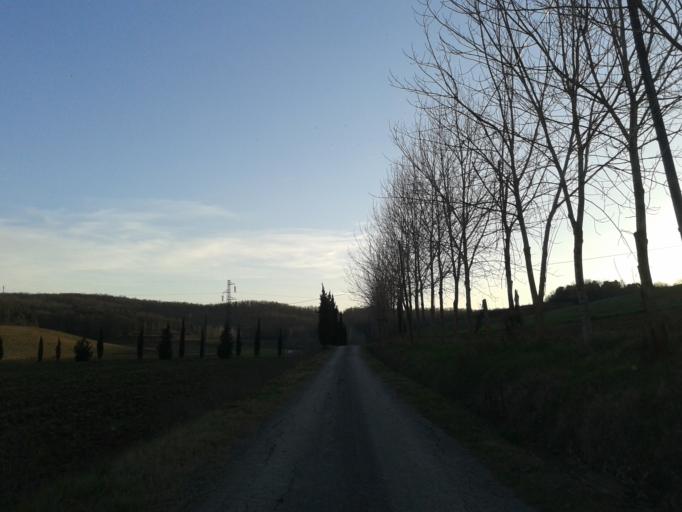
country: IT
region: Tuscany
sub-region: Provincia di Livorno
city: Guasticce
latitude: 43.5862
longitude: 10.4083
